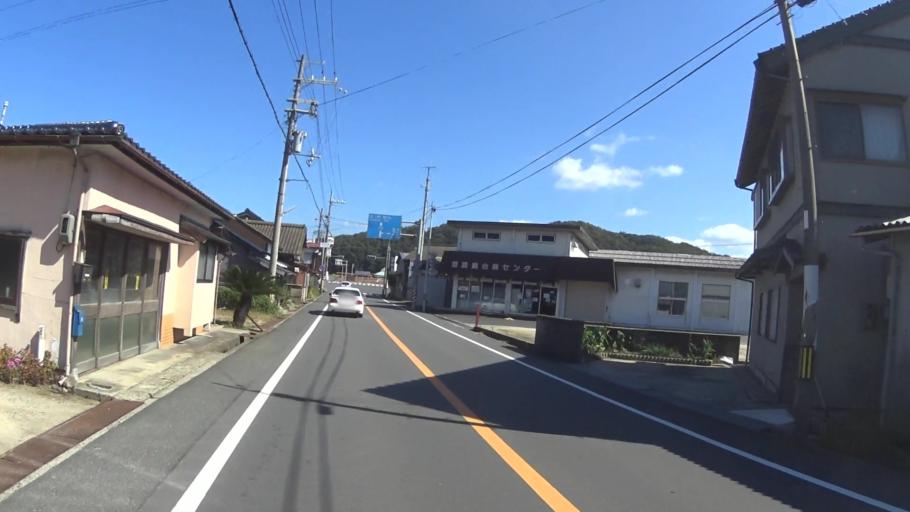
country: JP
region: Kyoto
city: Miyazu
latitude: 35.6684
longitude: 135.0260
